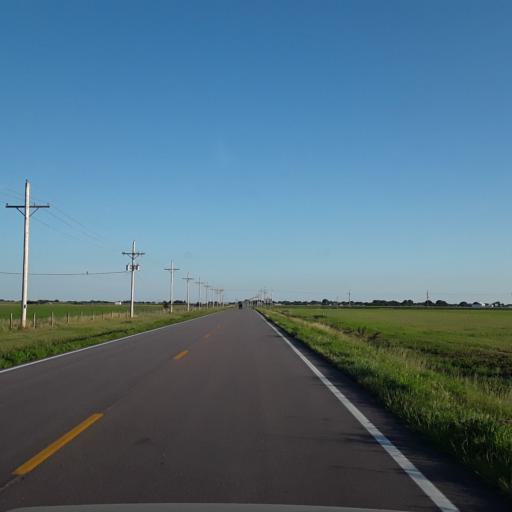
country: US
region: Nebraska
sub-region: Hall County
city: Grand Island
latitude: 40.9637
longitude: -98.3209
